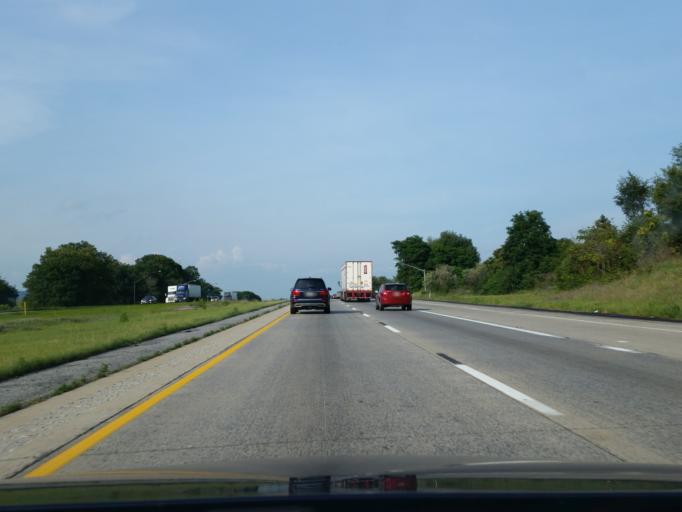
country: US
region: Pennsylvania
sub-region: Dauphin County
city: Skyline View
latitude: 40.3716
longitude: -76.6819
